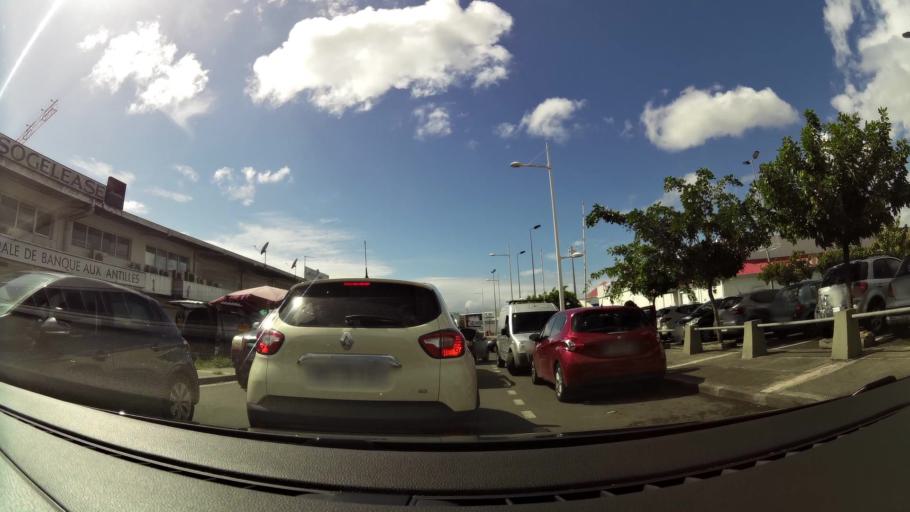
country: GP
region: Guadeloupe
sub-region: Guadeloupe
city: Pointe-a-Pitre
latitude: 16.2523
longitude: -61.5406
